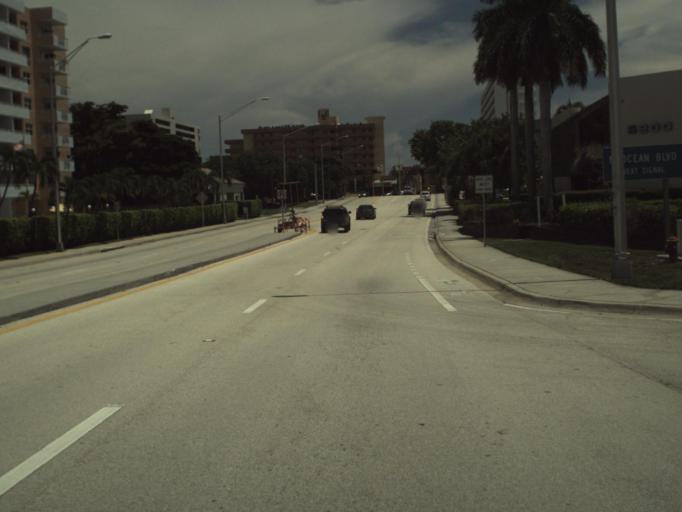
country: US
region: Florida
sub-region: Broward County
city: Lighthouse Point
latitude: 26.2502
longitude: -80.0891
